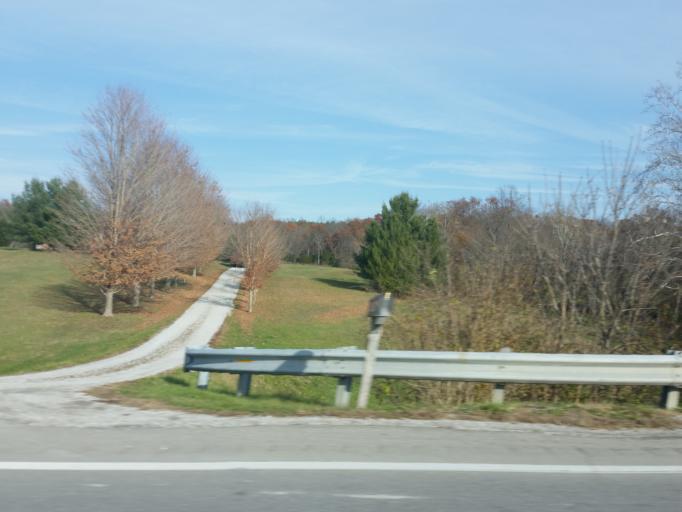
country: US
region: Kentucky
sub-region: Campbell County
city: Claryville
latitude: 38.8414
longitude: -84.3730
